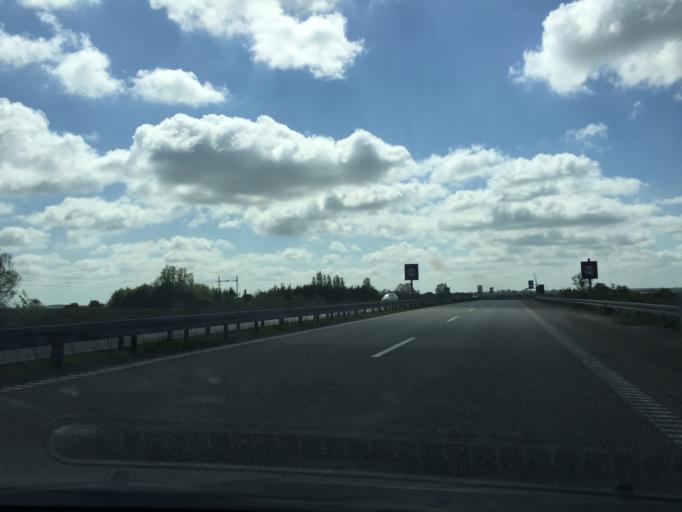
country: DK
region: Zealand
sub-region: Guldborgsund Kommune
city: Sundby
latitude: 54.8375
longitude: 11.8102
